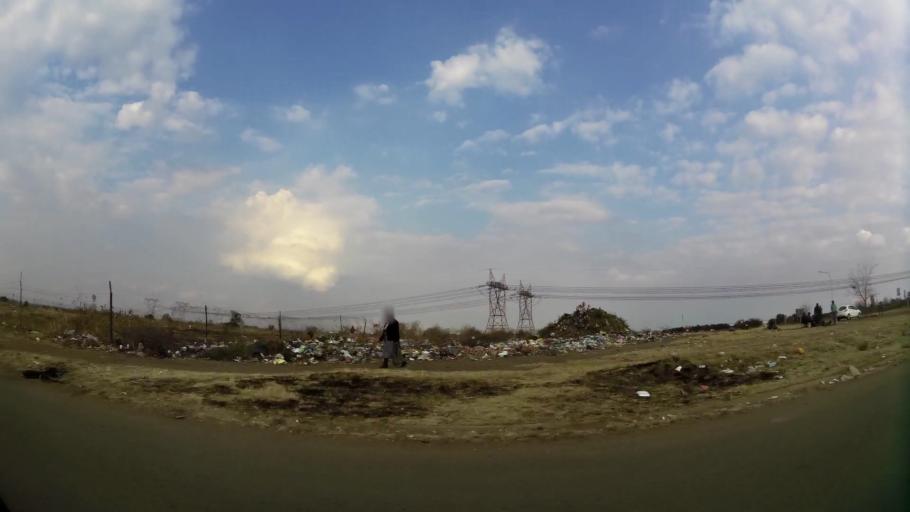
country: ZA
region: Gauteng
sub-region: Sedibeng District Municipality
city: Vanderbijlpark
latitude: -26.6960
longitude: 27.8768
